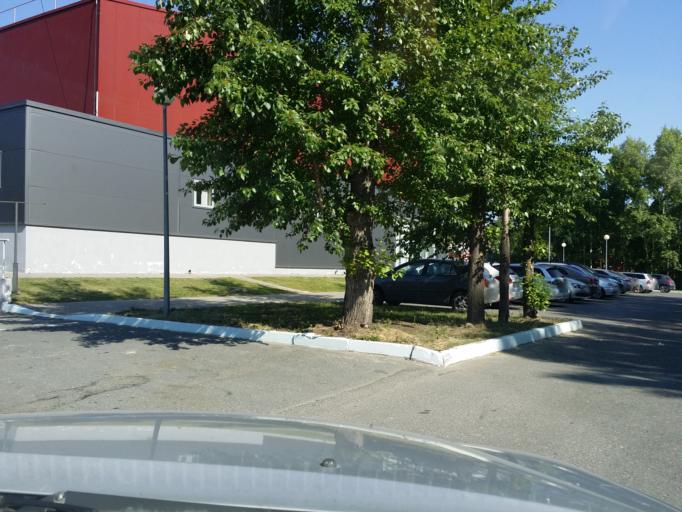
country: RU
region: Tomsk
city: Strezhevoy
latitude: 60.7254
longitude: 77.6044
